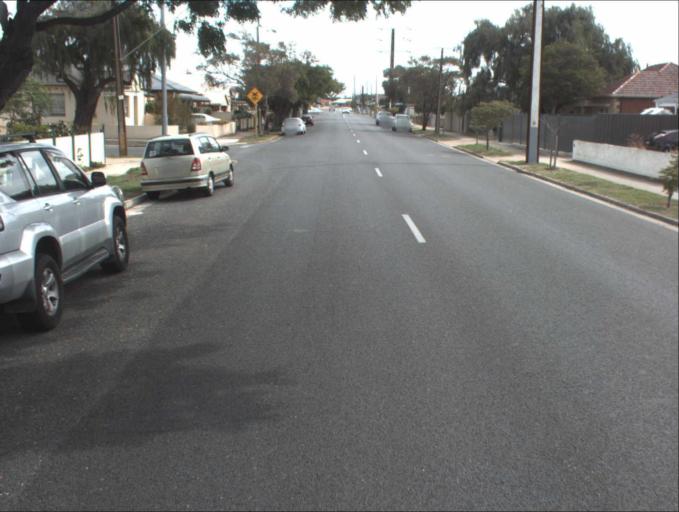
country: AU
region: South Australia
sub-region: Port Adelaide Enfield
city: Birkenhead
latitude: -34.8225
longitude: 138.4946
